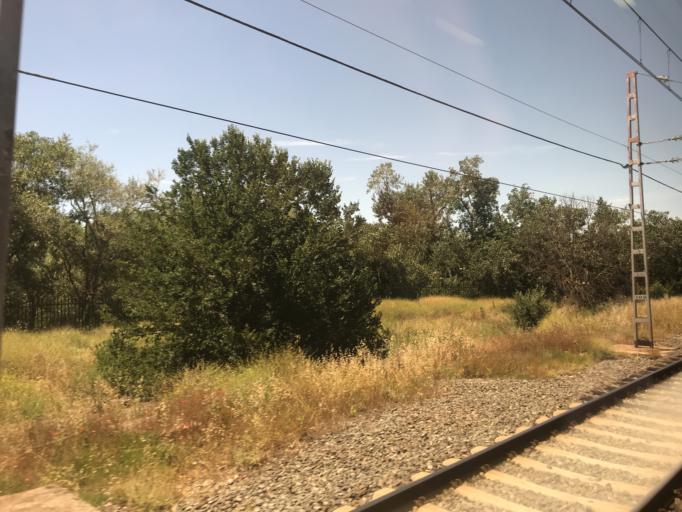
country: ES
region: Madrid
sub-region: Provincia de Madrid
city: Aranjuez
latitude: 40.0392
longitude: -3.6200
